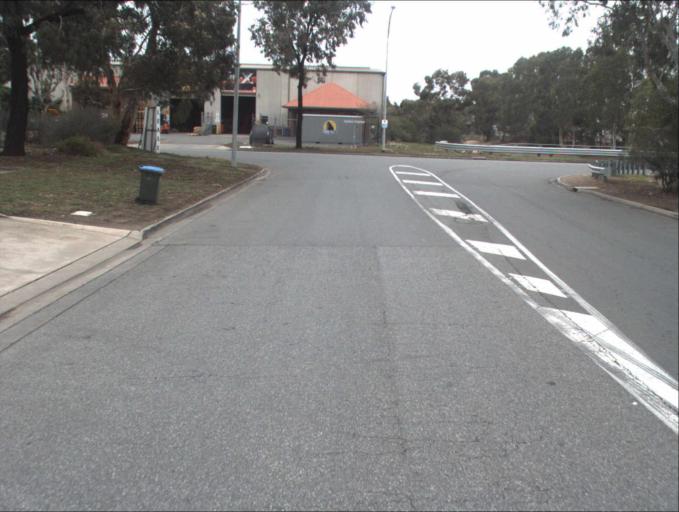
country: AU
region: South Australia
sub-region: Port Adelaide Enfield
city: Blair Athol
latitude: -34.8474
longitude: 138.5689
